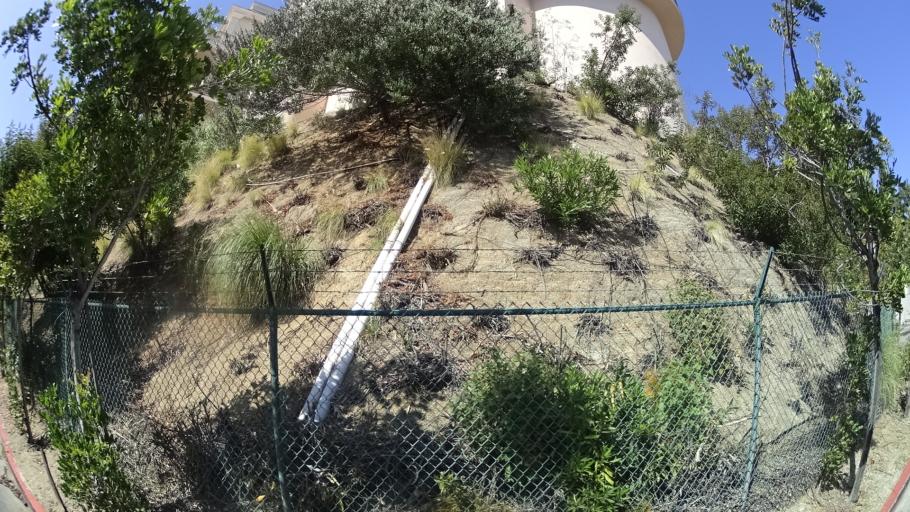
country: US
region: California
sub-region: Los Angeles County
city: West Hollywood
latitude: 34.0960
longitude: -118.3823
